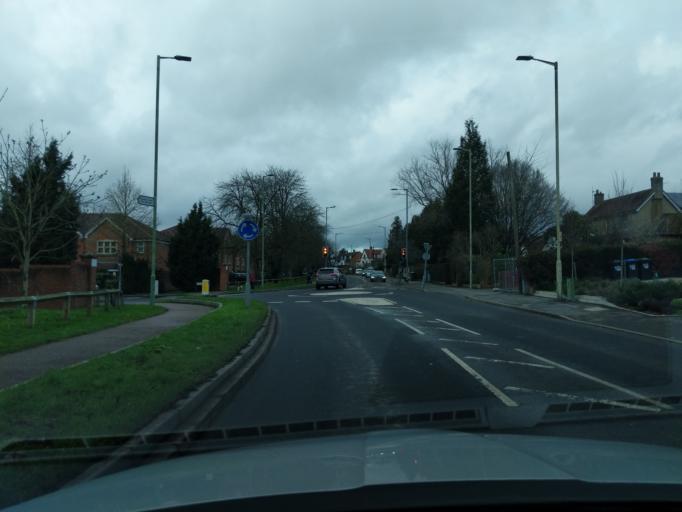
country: GB
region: England
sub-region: Hertfordshire
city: Kings Langley
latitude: 51.7338
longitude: -0.4576
